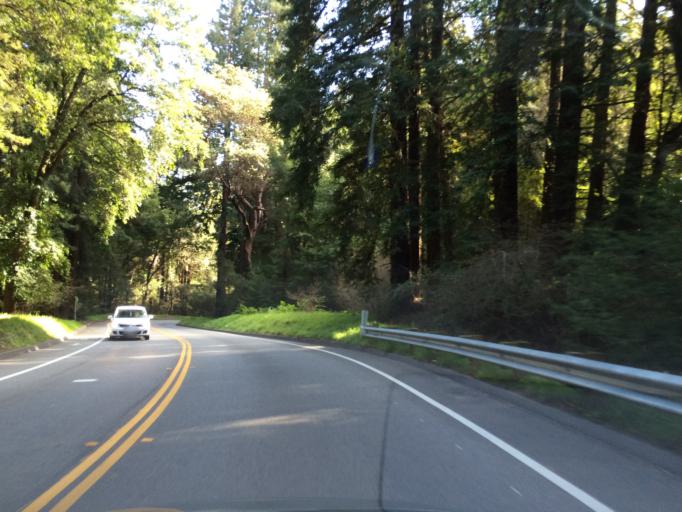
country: US
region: California
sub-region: Santa Cruz County
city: Pasatiempo
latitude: 36.9962
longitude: -122.0636
